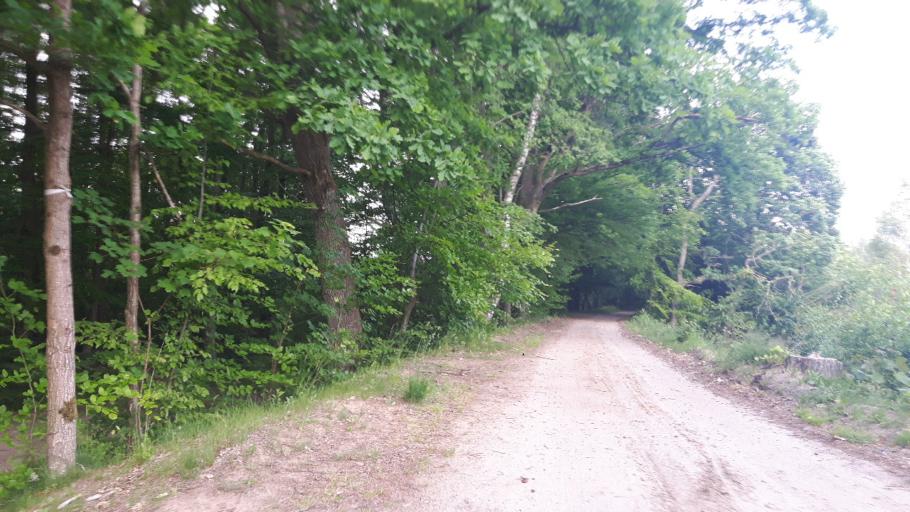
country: PL
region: Pomeranian Voivodeship
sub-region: Slupsk
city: Slupsk
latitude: 54.6122
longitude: 17.0245
